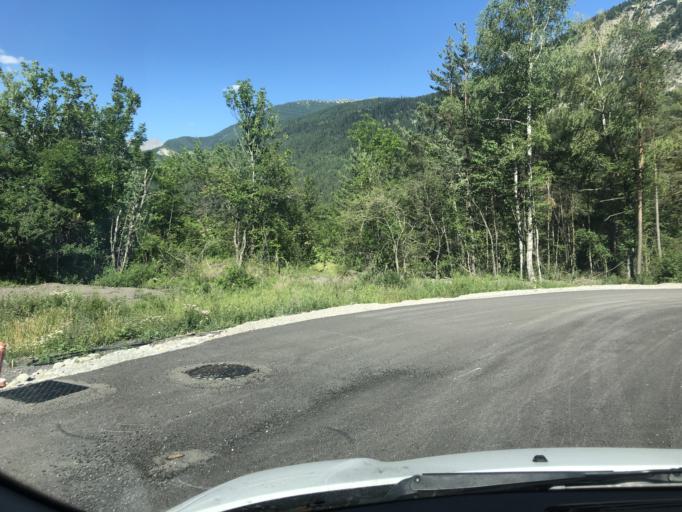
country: FR
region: Provence-Alpes-Cote d'Azur
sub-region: Departement des Alpes-de-Haute-Provence
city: Annot
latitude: 44.1583
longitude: 6.5987
